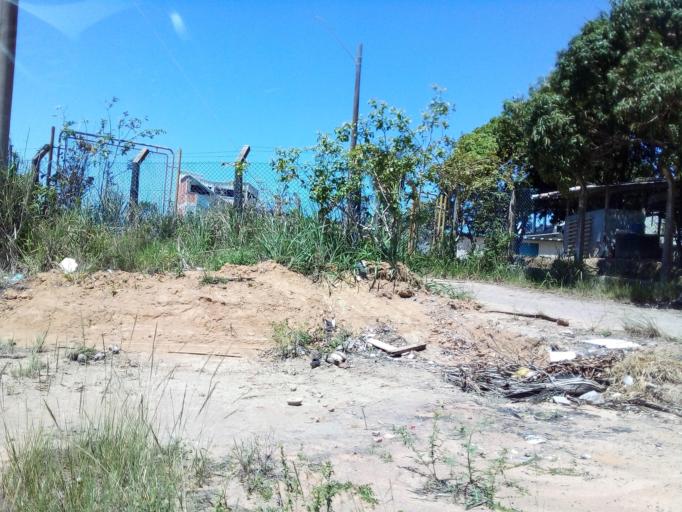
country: BR
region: Espirito Santo
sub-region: Aracruz
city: Aracruz
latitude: -19.8244
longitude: -40.0678
